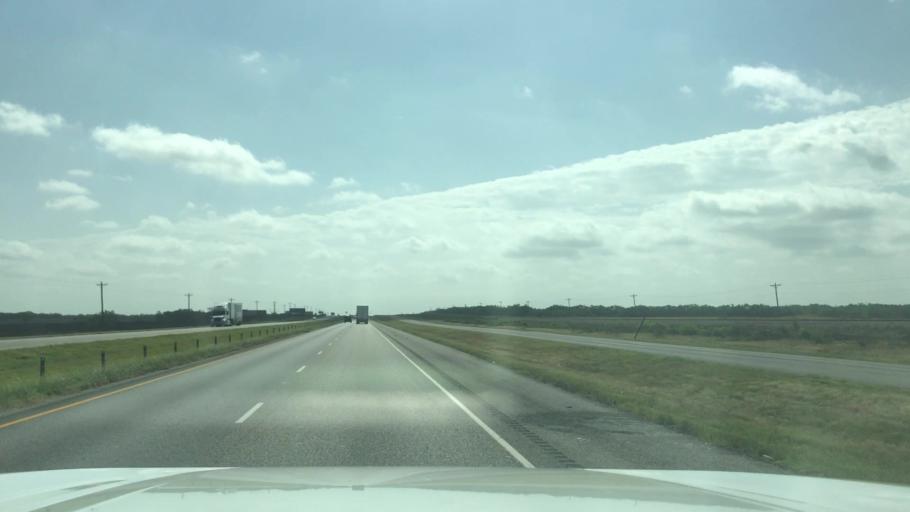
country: US
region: Texas
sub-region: Taylor County
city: Merkel
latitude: 32.4658
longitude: -99.9749
